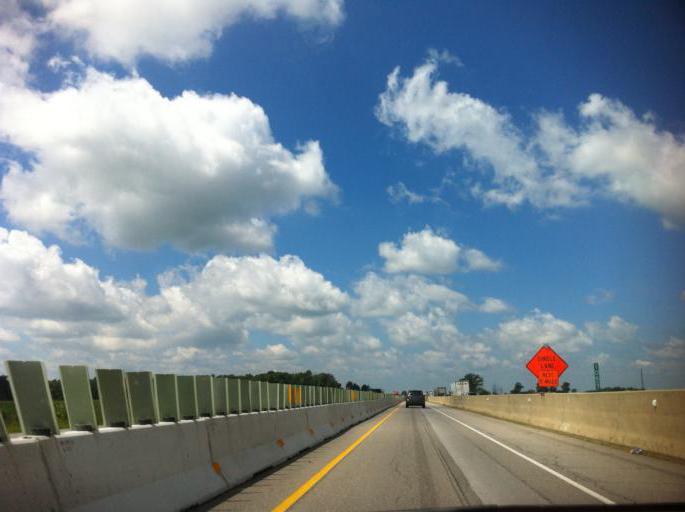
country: US
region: Ohio
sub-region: Huron County
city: Bellevue
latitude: 41.3509
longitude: -82.8506
